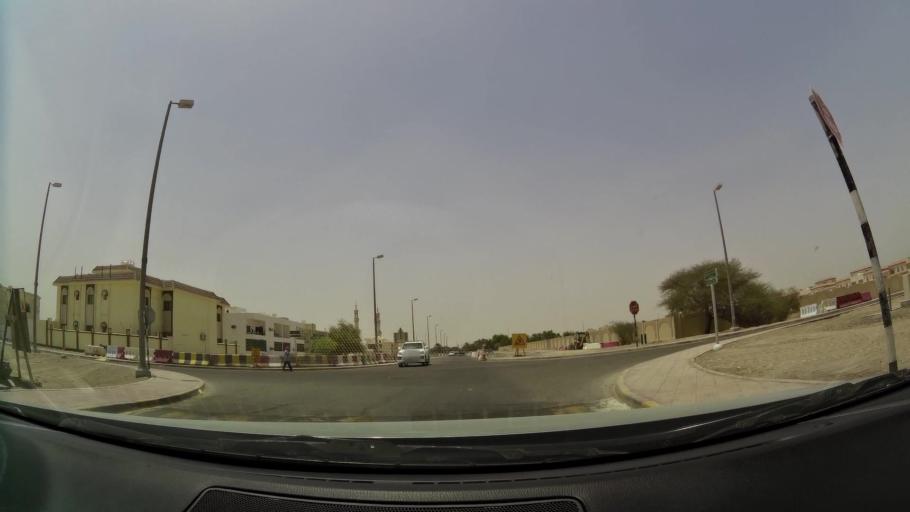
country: AE
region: Abu Dhabi
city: Al Ain
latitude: 24.2083
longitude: 55.7174
